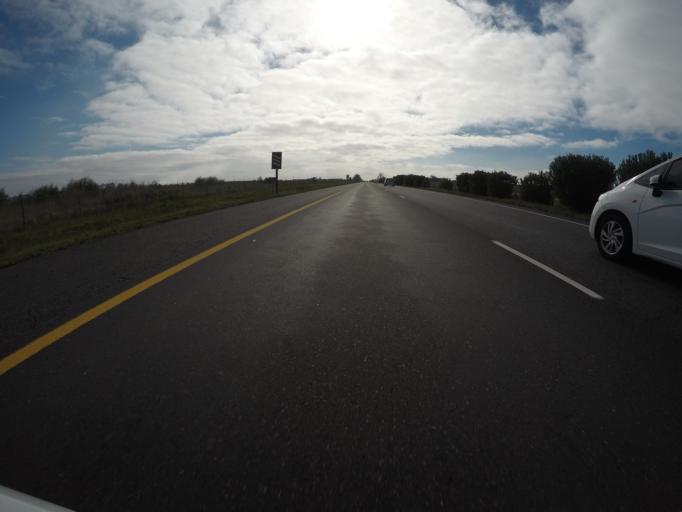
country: ZA
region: Western Cape
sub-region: City of Cape Town
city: Kraaifontein
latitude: -33.8298
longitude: 18.7556
